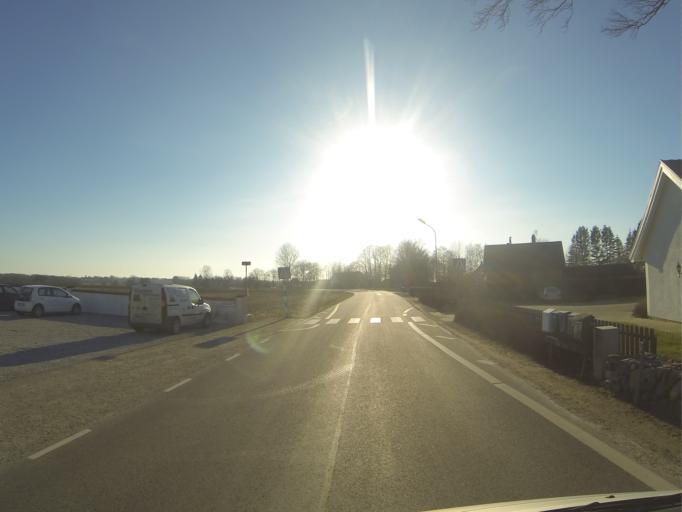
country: SE
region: Skane
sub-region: Horby Kommun
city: Hoerby
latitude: 55.8363
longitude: 13.6203
